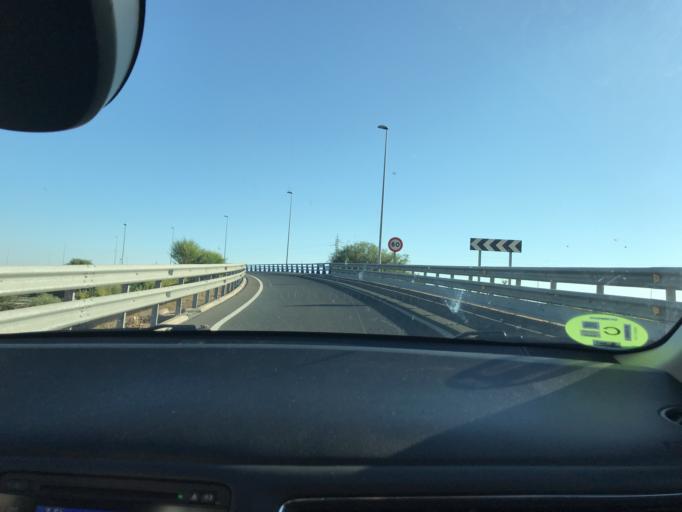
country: ES
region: Andalusia
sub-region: Provincia de Sevilla
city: Alcala de Guadaira
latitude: 37.4327
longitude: -5.8455
